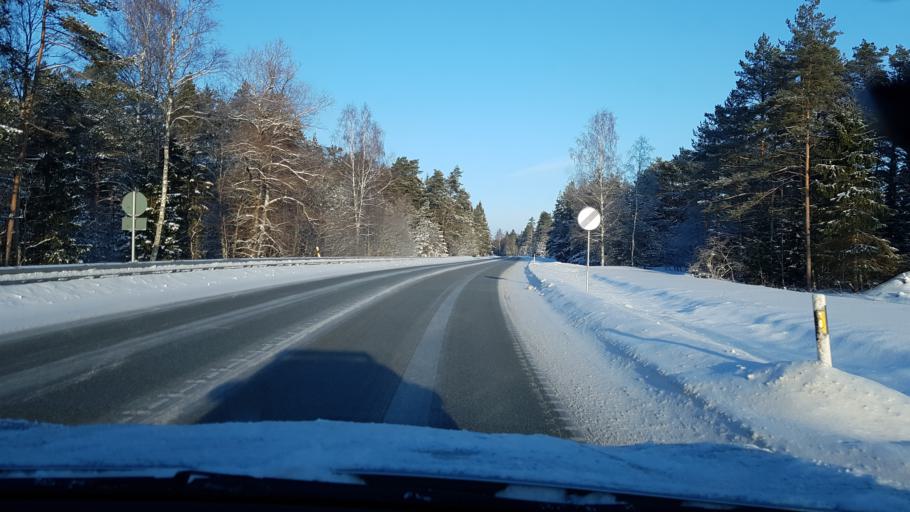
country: EE
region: Harju
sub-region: Keila linn
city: Keila
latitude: 59.2066
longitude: 24.4252
